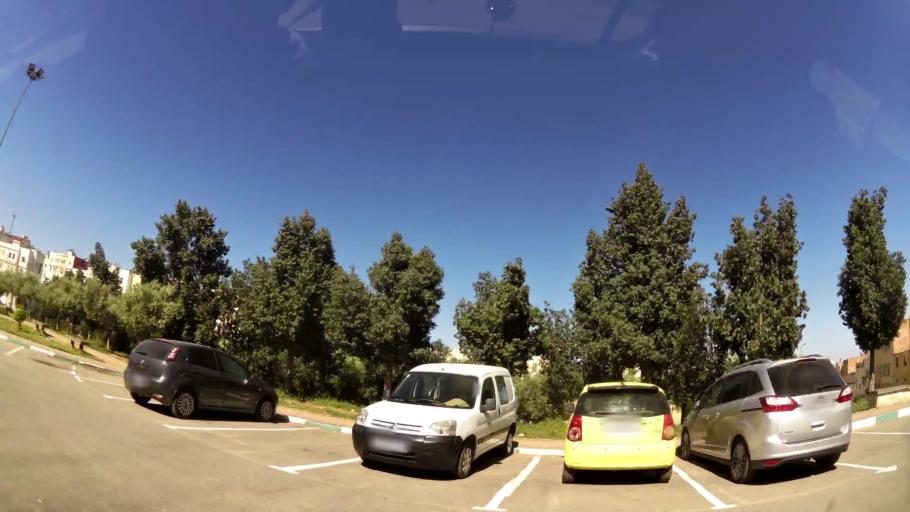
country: MA
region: Meknes-Tafilalet
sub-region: Meknes
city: Meknes
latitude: 33.9071
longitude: -5.5391
